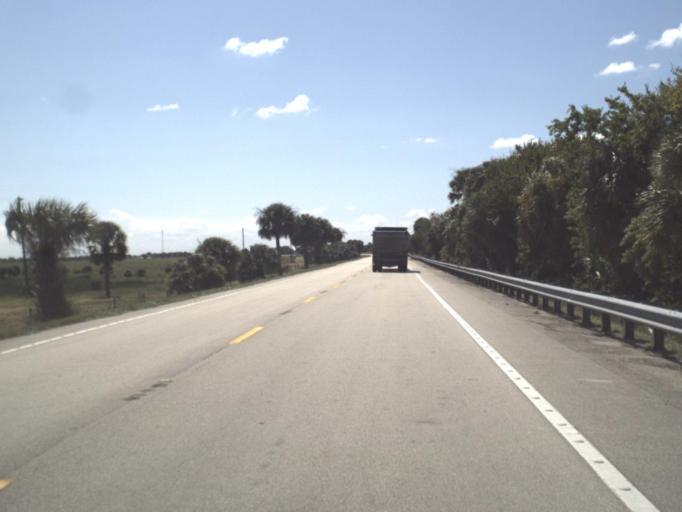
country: US
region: Florida
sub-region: Glades County
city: Buckhead Ridge
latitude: 27.0831
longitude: -80.9686
